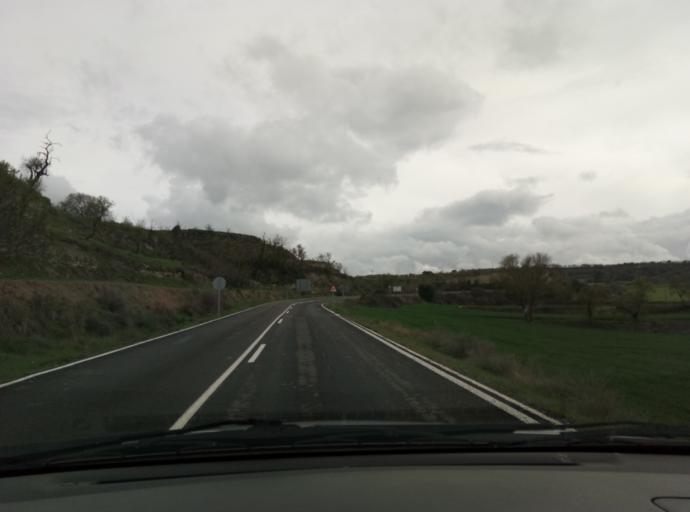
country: ES
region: Catalonia
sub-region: Provincia de Lleida
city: Cervera
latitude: 41.6250
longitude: 1.3398
